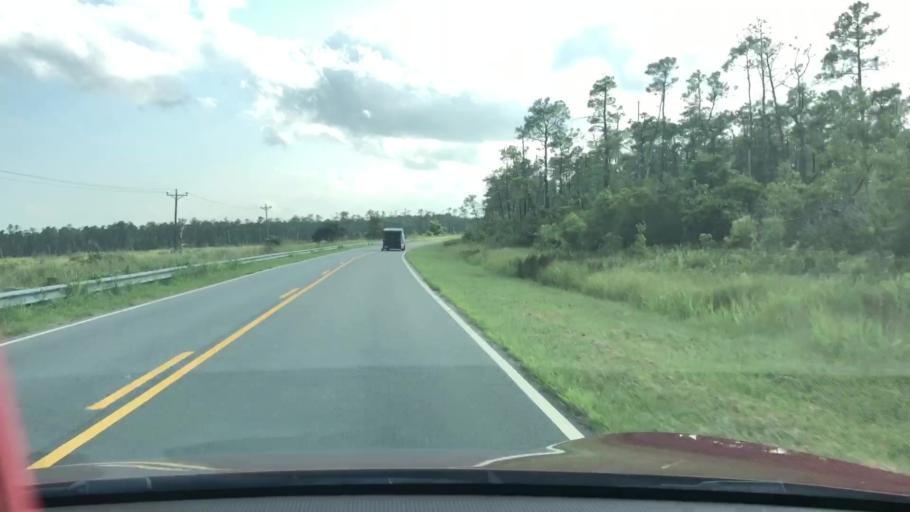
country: US
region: North Carolina
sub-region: Dare County
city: Wanchese
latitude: 35.6107
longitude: -75.7977
